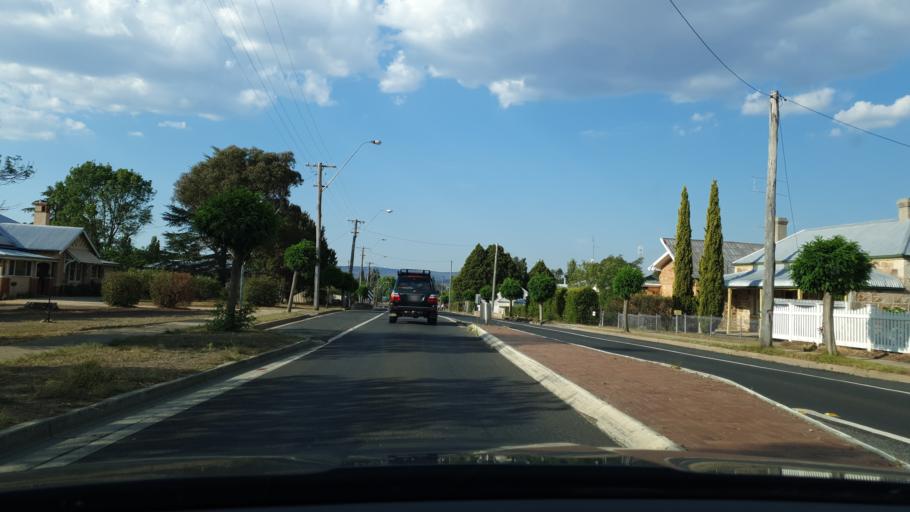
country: AU
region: New South Wales
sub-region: Tenterfield Municipality
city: Carrolls Creek
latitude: -29.0493
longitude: 152.0199
